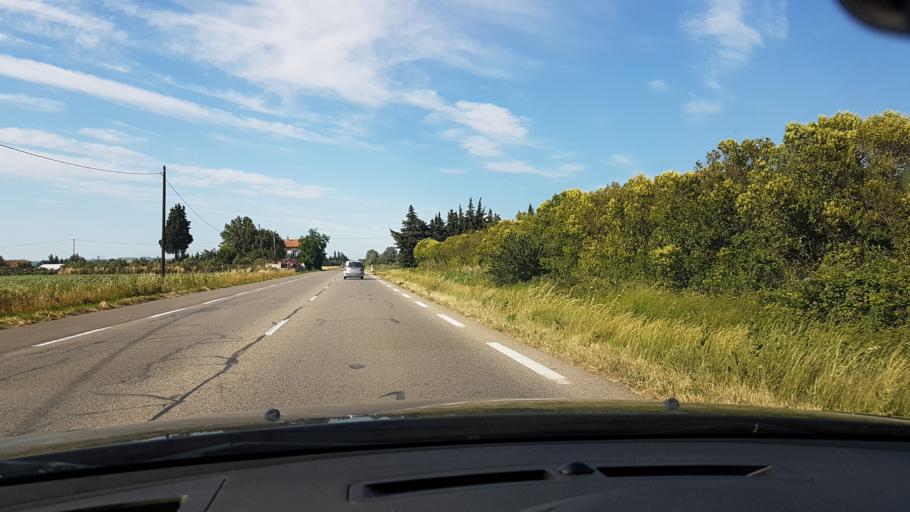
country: FR
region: Provence-Alpes-Cote d'Azur
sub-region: Departement des Bouches-du-Rhone
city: Fontvieille
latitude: 43.7522
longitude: 4.6810
